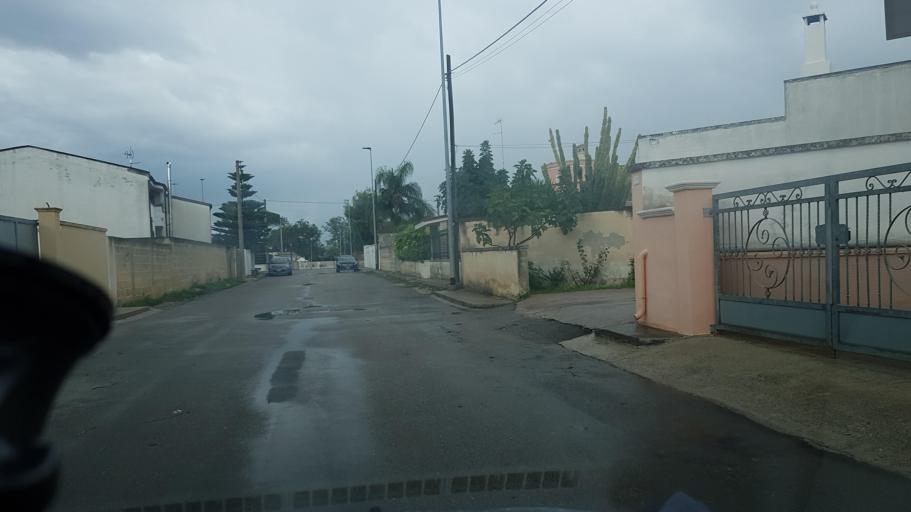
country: IT
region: Apulia
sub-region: Provincia di Lecce
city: Carmiano
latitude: 40.3412
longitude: 18.0494
